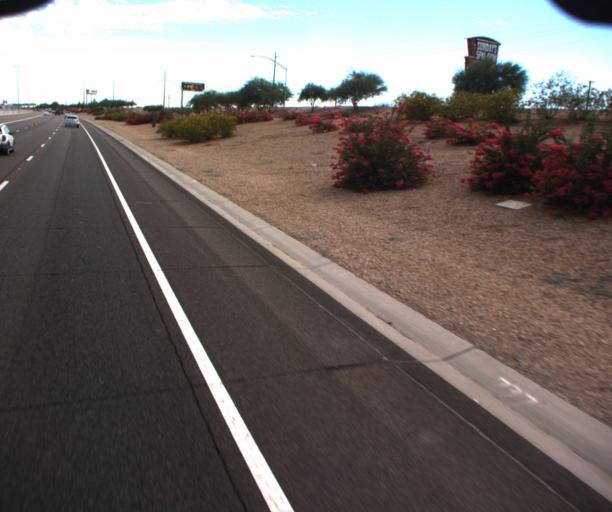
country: US
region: Arizona
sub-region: Maricopa County
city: Guadalupe
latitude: 33.2919
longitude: -111.9443
